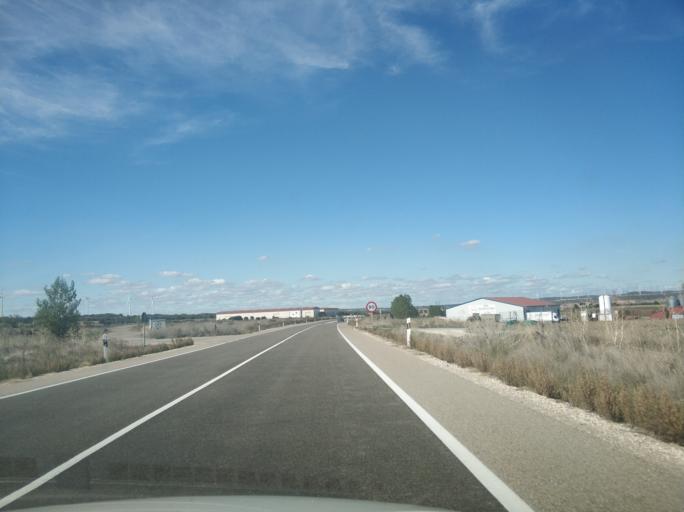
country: ES
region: Castille and Leon
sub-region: Provincia de Burgos
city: Hontoria de la Cantera
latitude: 42.2001
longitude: -3.6476
